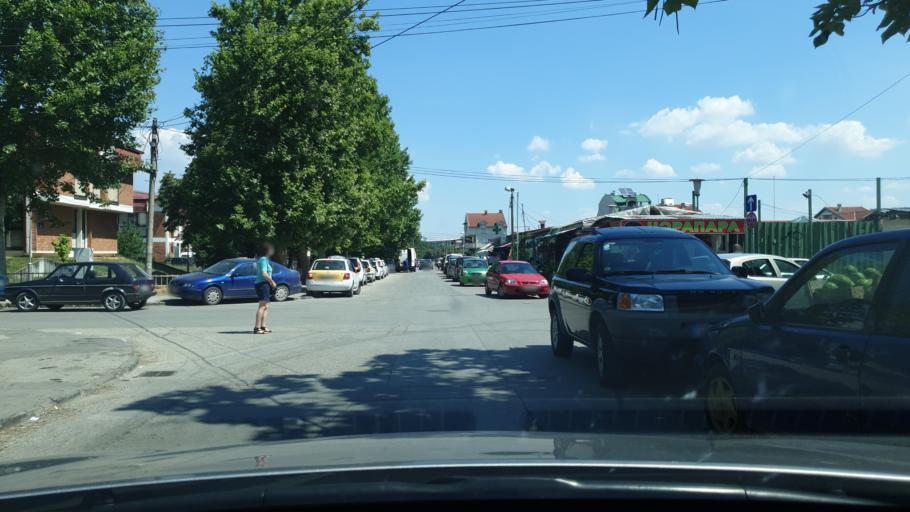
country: MK
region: Kisela Voda
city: Kisela Voda
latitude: 41.9385
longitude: 21.5151
